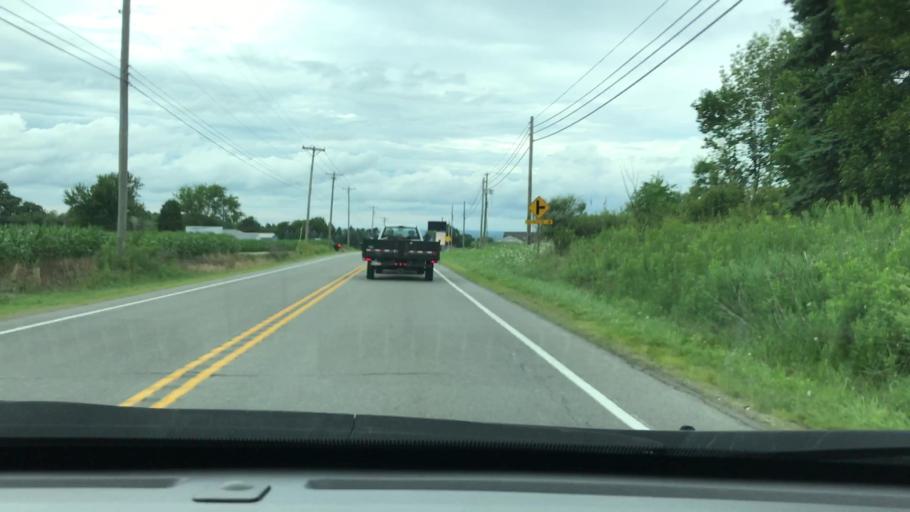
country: US
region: Pennsylvania
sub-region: Elk County
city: Ridgway
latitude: 41.4016
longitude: -78.7025
